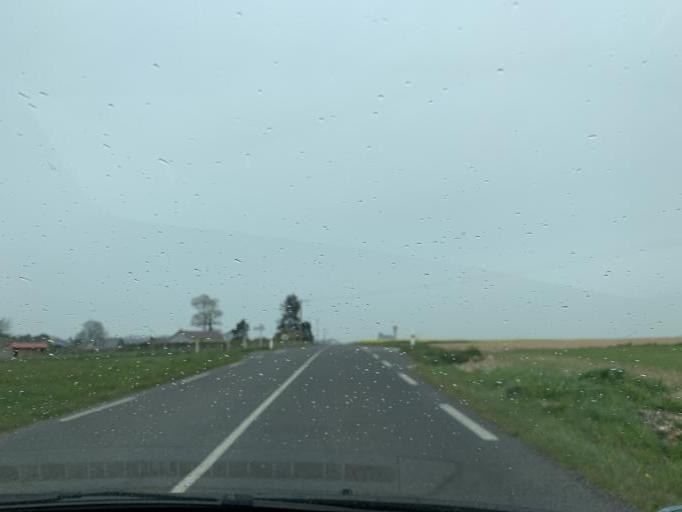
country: FR
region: Haute-Normandie
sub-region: Departement de la Seine-Maritime
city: Cany-Barville
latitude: 49.8095
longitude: 0.6684
